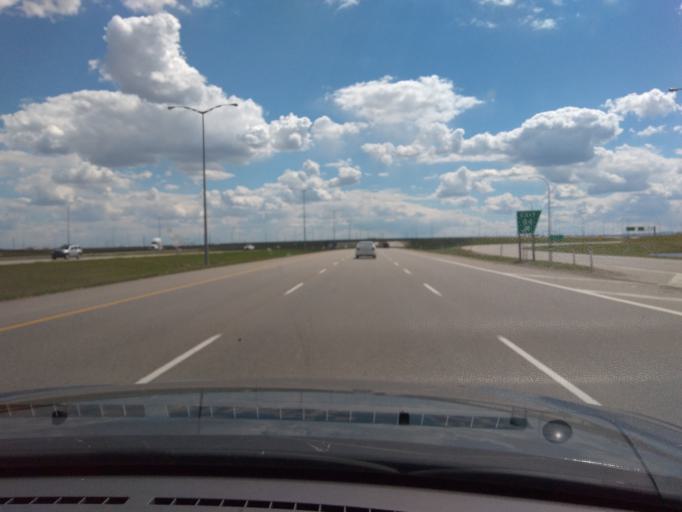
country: CA
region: Alberta
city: Chestermere
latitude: 51.0212
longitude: -113.9212
